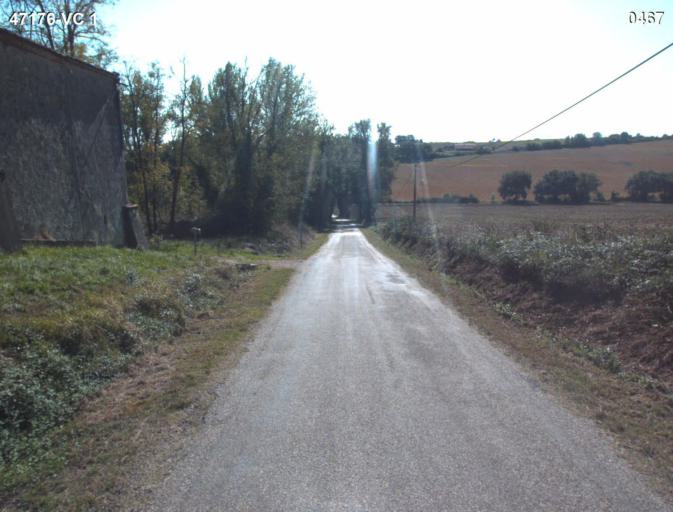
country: FR
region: Aquitaine
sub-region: Departement du Lot-et-Garonne
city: Lavardac
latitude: 44.1971
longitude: 0.2928
